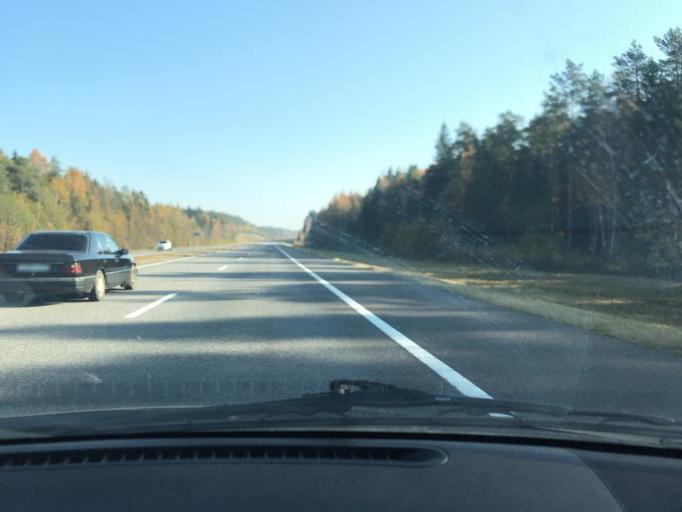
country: BY
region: Minsk
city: Bobr
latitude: 54.3934
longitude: 29.4071
